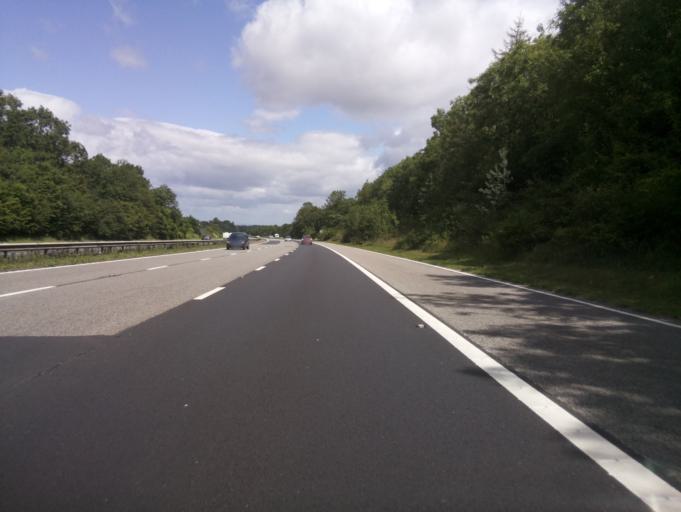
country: GB
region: England
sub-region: South Gloucestershire
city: Falfield
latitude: 51.6132
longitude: -2.4643
